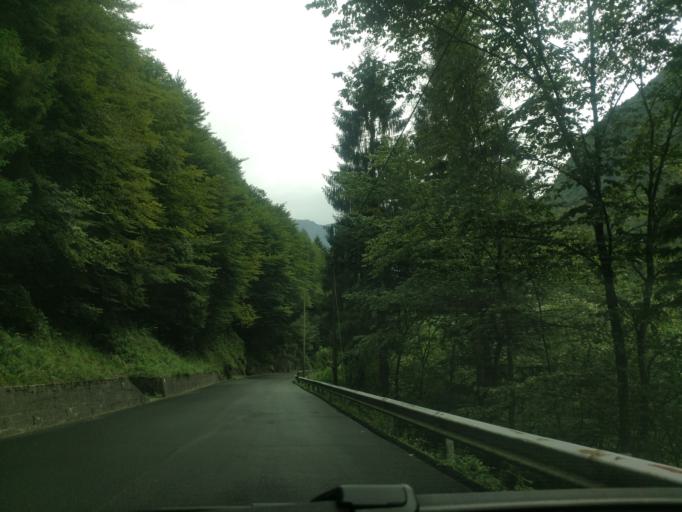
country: IT
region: Veneto
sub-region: Provincia di Belluno
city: Longarone
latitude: 46.2863
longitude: 12.2407
